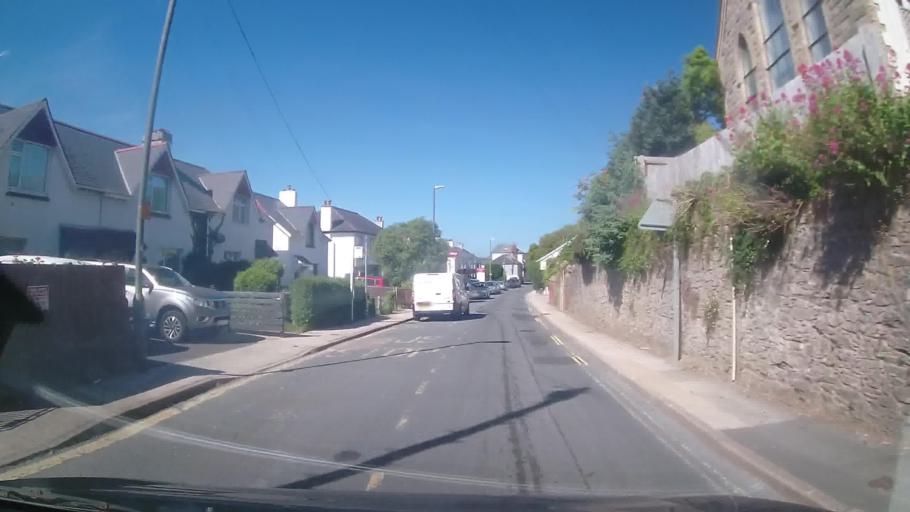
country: GB
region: England
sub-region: Borough of Torbay
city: Brixham
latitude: 50.3843
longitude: -3.5231
